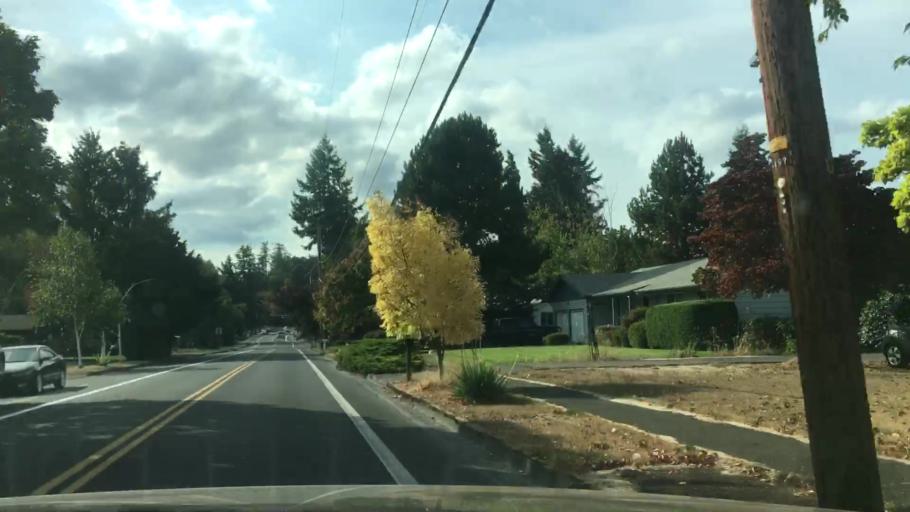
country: US
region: Oregon
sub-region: Lane County
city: Eugene
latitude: 44.0841
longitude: -123.0898
